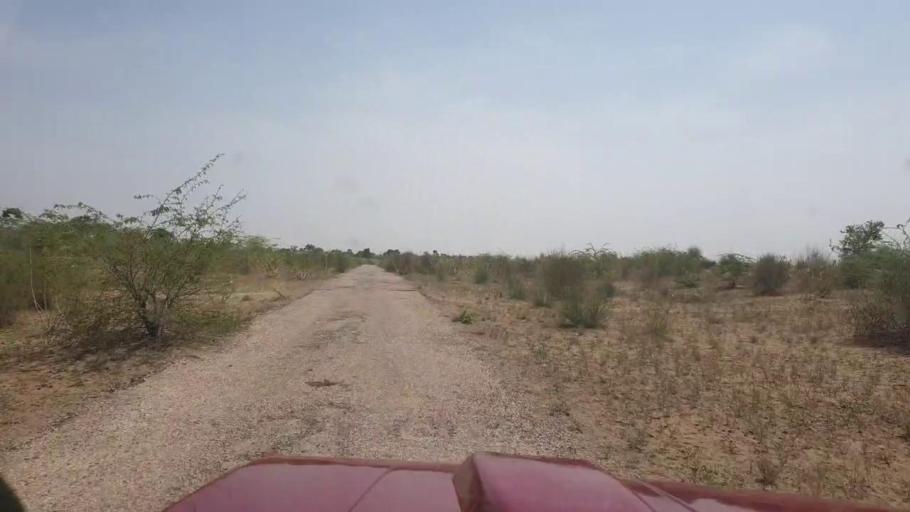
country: PK
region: Sindh
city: Islamkot
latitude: 25.1169
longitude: 70.3770
